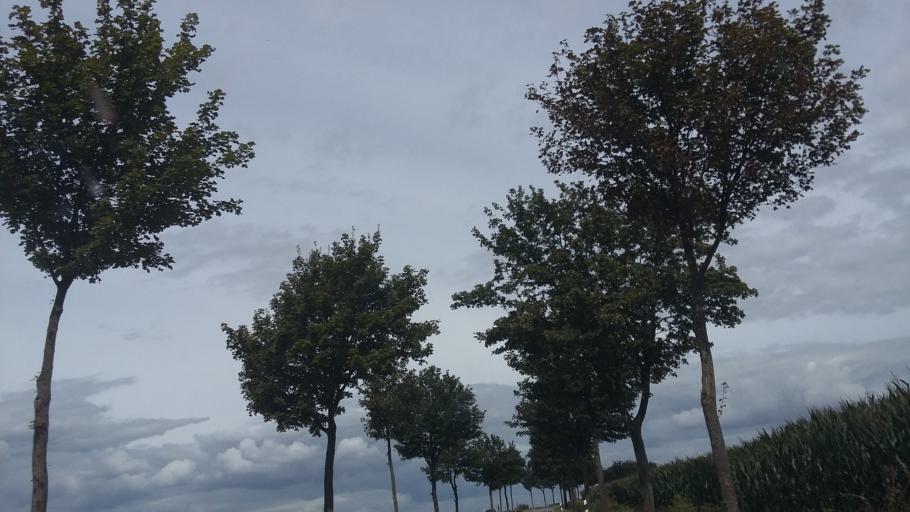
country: DE
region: Lower Saxony
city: Harsum
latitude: 52.1931
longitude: 10.0073
